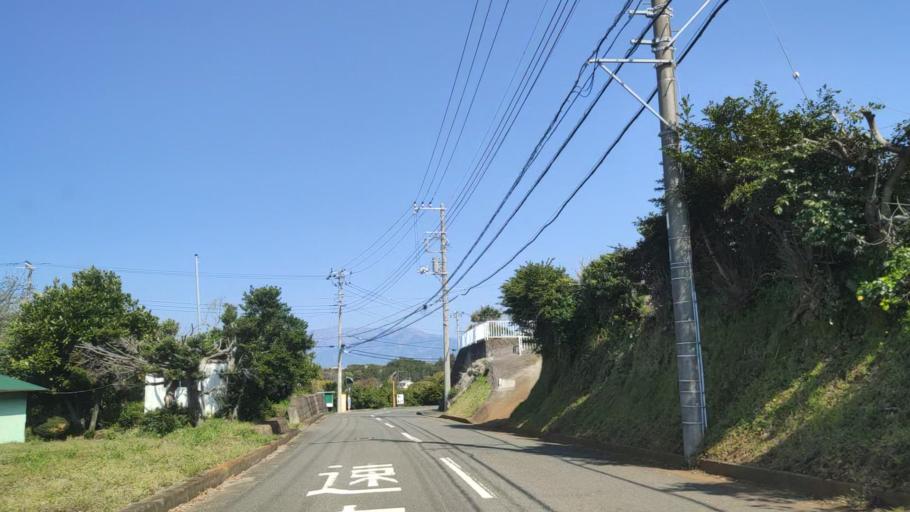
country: JP
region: Kanagawa
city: Ninomiya
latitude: 35.3233
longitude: 139.2582
